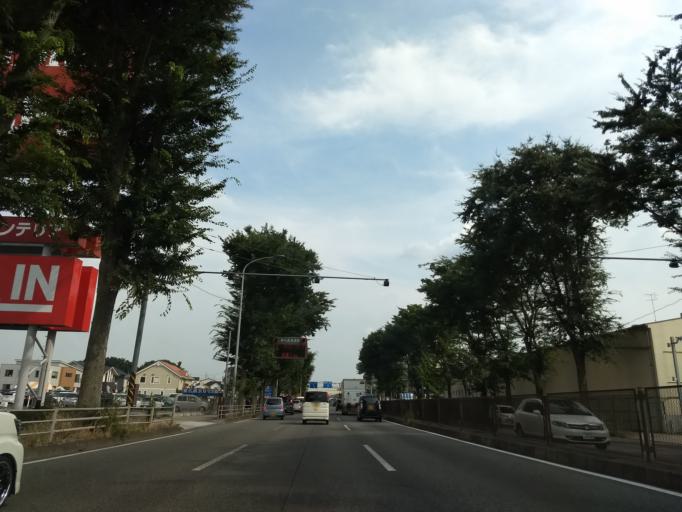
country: JP
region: Tokyo
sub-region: Machida-shi
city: Machida
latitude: 35.5203
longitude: 139.4525
